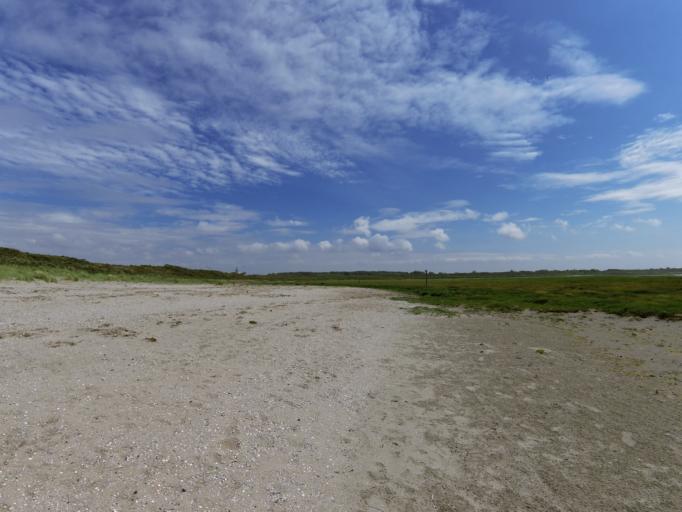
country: NL
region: South Holland
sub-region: Gemeente Rotterdam
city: Hoek van Holland
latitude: 51.9185
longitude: 4.0526
